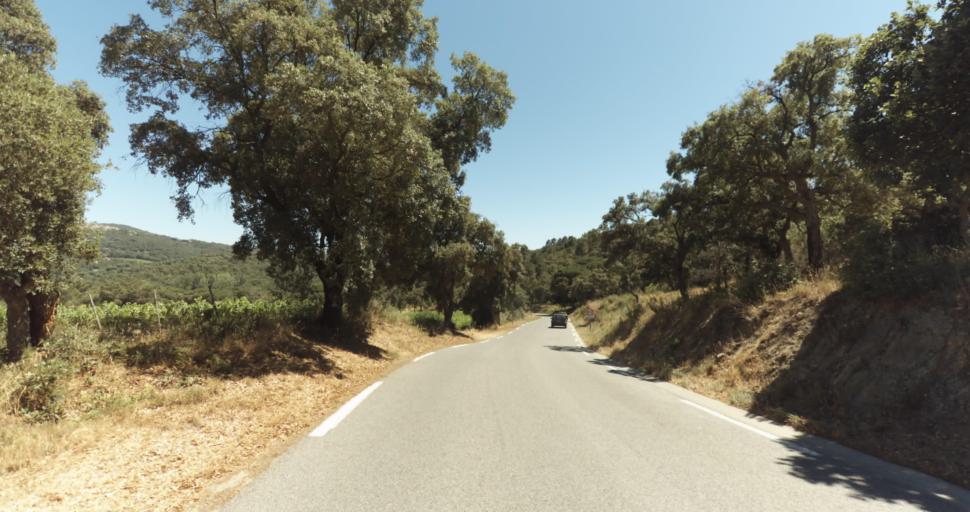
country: FR
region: Provence-Alpes-Cote d'Azur
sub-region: Departement du Var
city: Gassin
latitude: 43.2412
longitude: 6.5630
